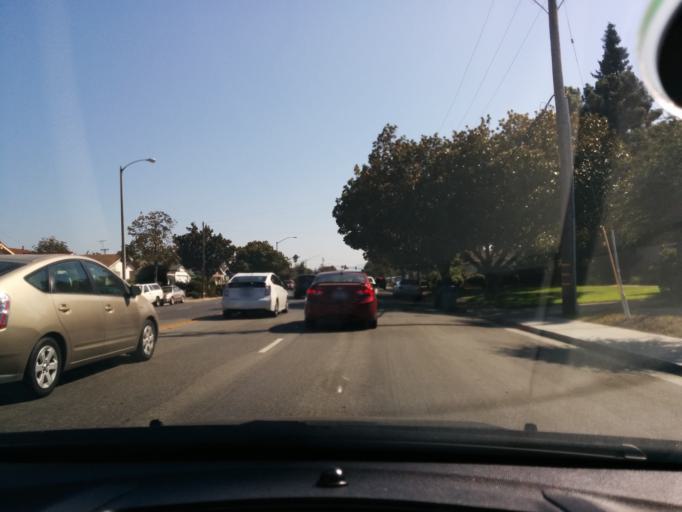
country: US
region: California
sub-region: Santa Clara County
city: Sunnyvale
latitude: 37.3645
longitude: -122.0143
